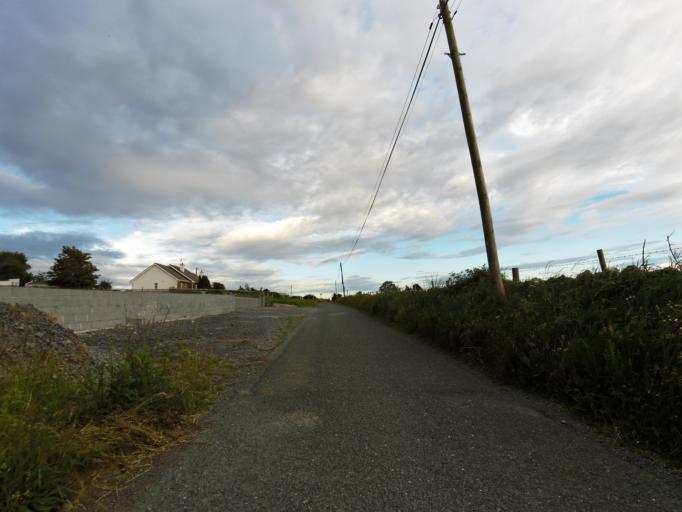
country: IE
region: Connaught
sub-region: County Galway
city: Athenry
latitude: 53.2924
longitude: -8.7207
